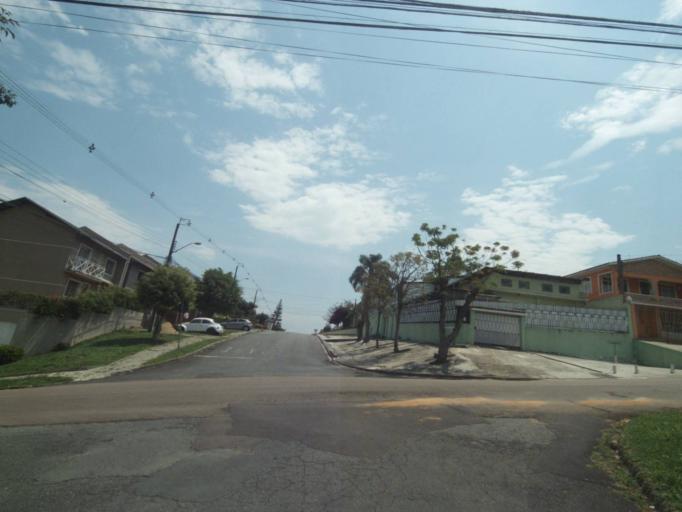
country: BR
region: Parana
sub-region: Pinhais
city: Pinhais
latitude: -25.4201
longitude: -49.2092
